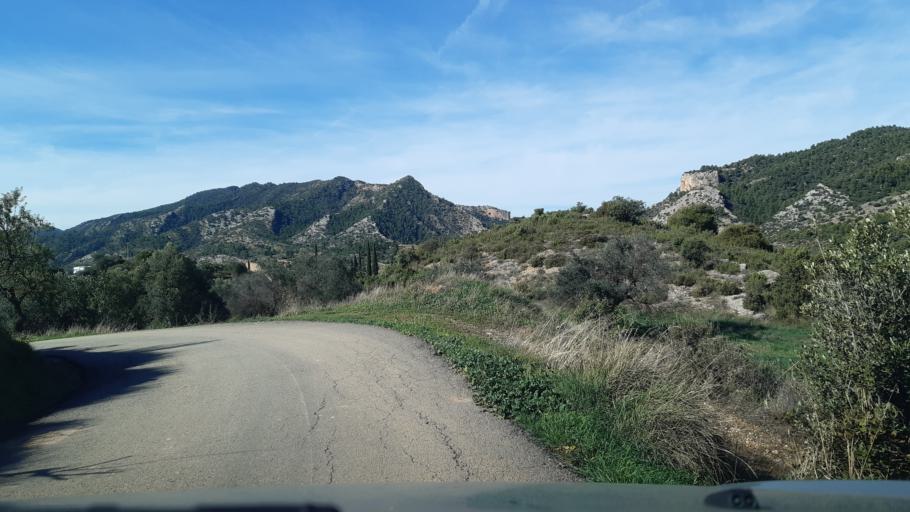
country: ES
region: Aragon
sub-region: Provincia de Teruel
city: Valderrobres
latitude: 40.8359
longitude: 0.1947
